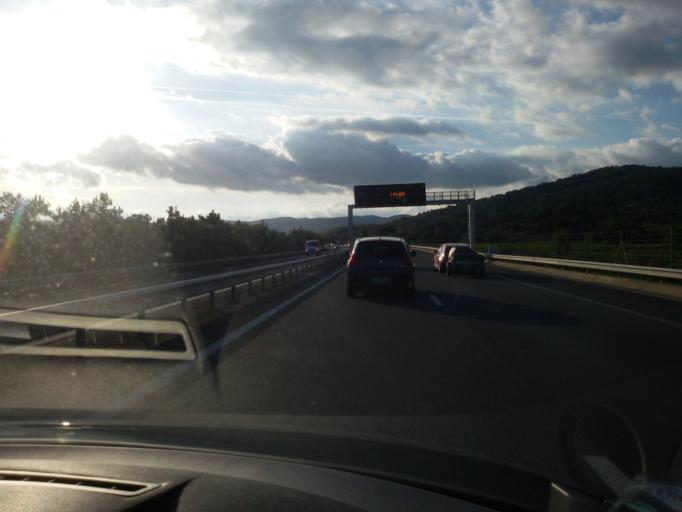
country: FR
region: Languedoc-Roussillon
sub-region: Departement de l'Herault
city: Lodeve
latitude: 43.6833
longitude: 3.3728
